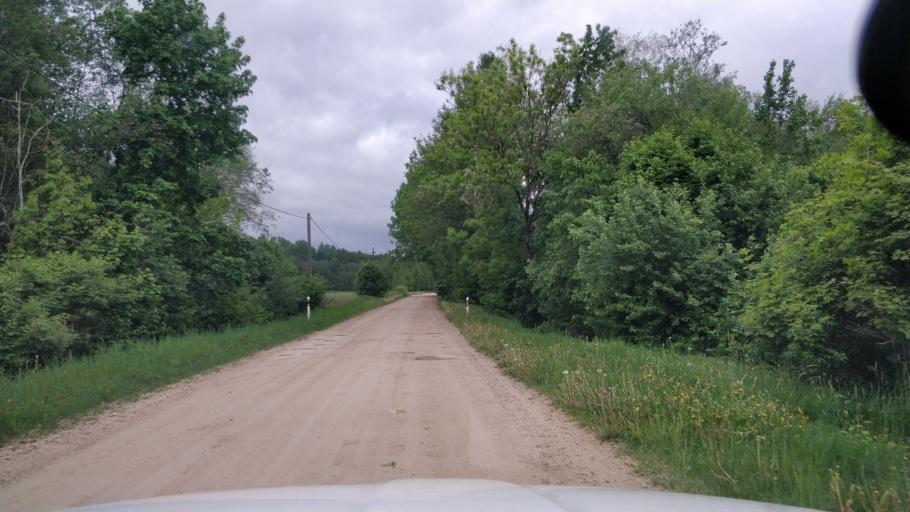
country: EE
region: Paernumaa
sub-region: Halinga vald
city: Parnu-Jaagupi
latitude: 58.7098
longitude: 24.3231
